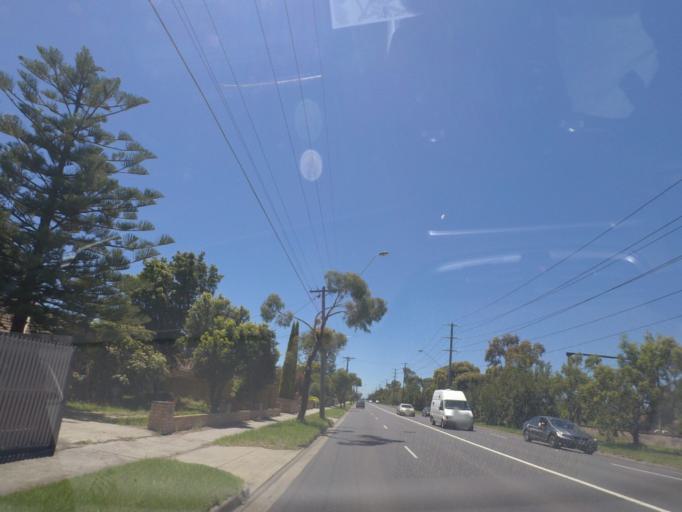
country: AU
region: Victoria
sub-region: Darebin
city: Reservoir
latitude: -37.7023
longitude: 145.0101
